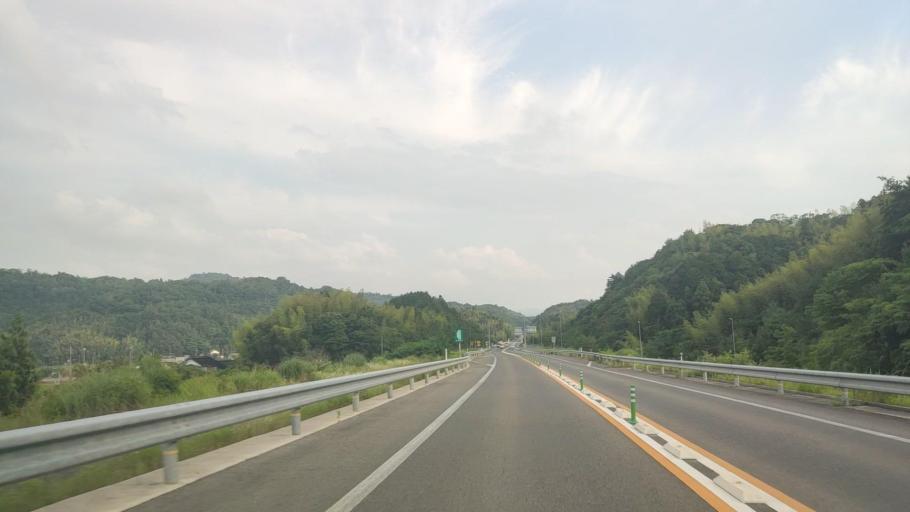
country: JP
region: Tottori
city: Kurayoshi
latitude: 35.4663
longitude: 133.8084
